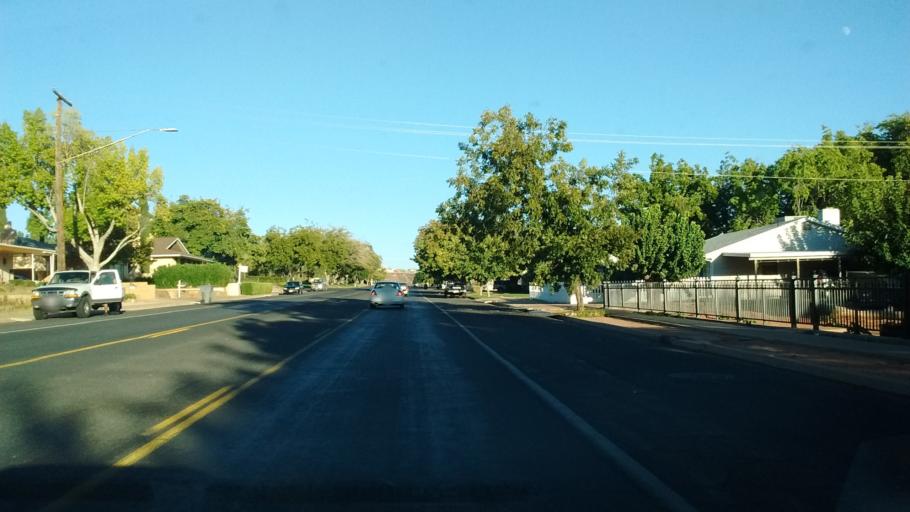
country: US
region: Utah
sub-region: Washington County
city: Saint George
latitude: 37.1065
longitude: -113.5721
